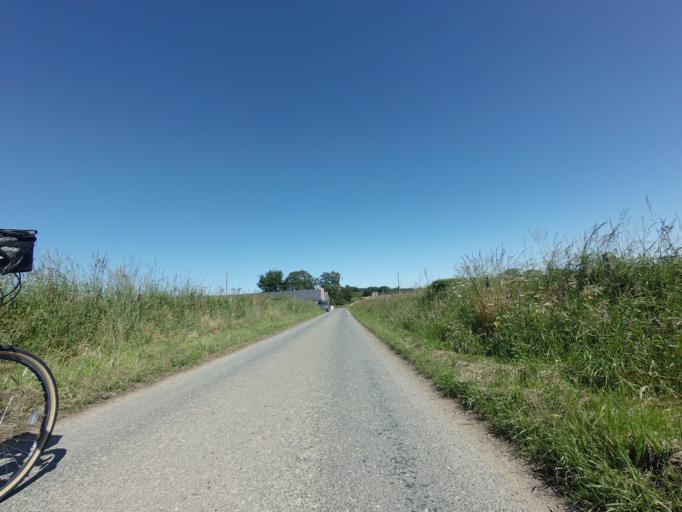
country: GB
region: Scotland
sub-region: Aberdeenshire
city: Macduff
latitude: 57.6309
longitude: -2.4848
